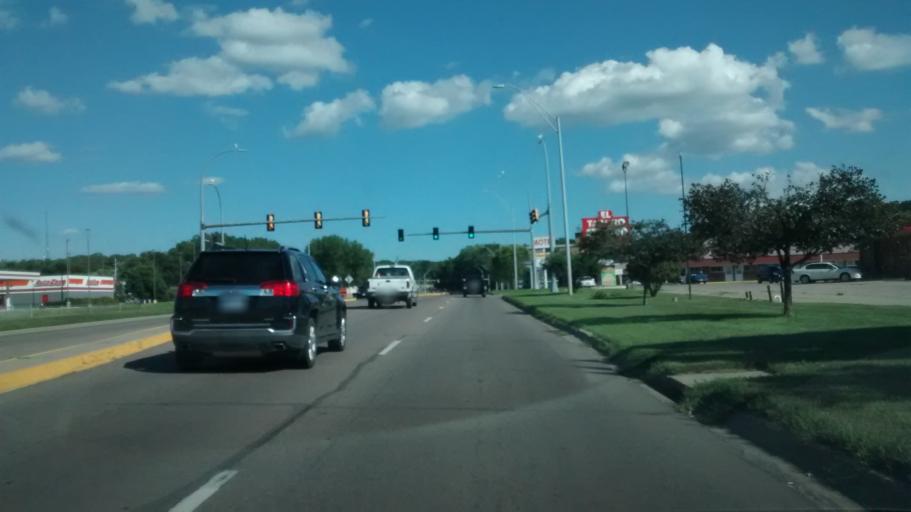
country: US
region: Iowa
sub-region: Woodbury County
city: Sioux City
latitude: 42.4879
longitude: -96.3647
